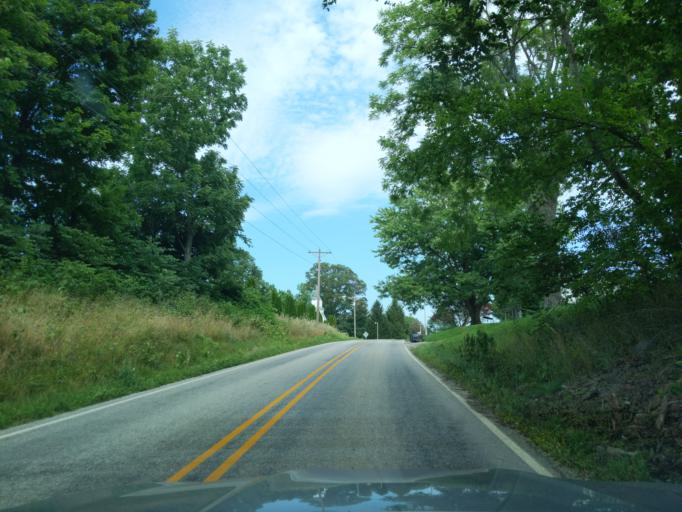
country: US
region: Indiana
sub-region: Ripley County
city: Osgood
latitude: 39.1976
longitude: -85.2451
